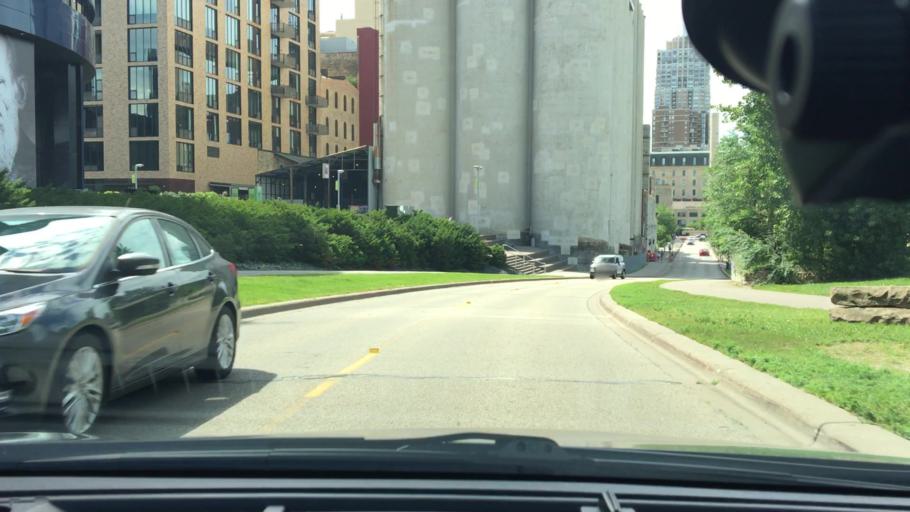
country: US
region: Minnesota
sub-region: Hennepin County
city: Minneapolis
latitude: 44.9786
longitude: -93.2551
